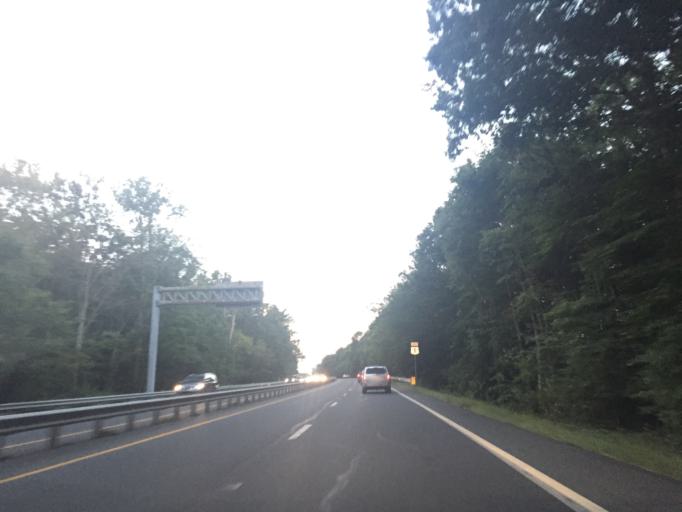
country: US
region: Maryland
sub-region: Harford County
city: Bel Air North
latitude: 39.5505
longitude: -76.3693
